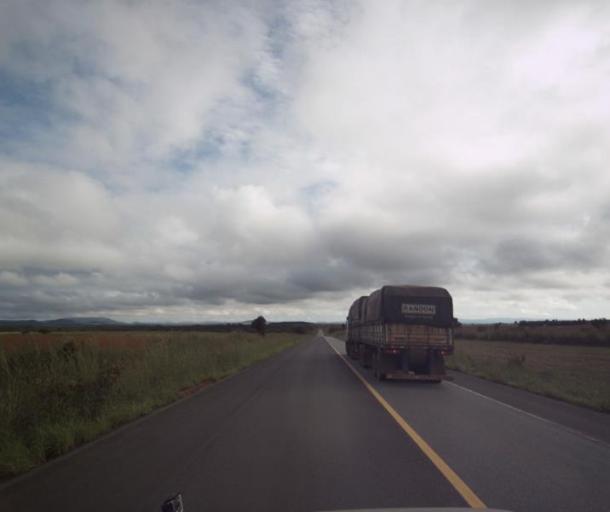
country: BR
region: Goias
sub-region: Padre Bernardo
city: Padre Bernardo
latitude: -15.3492
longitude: -48.6470
